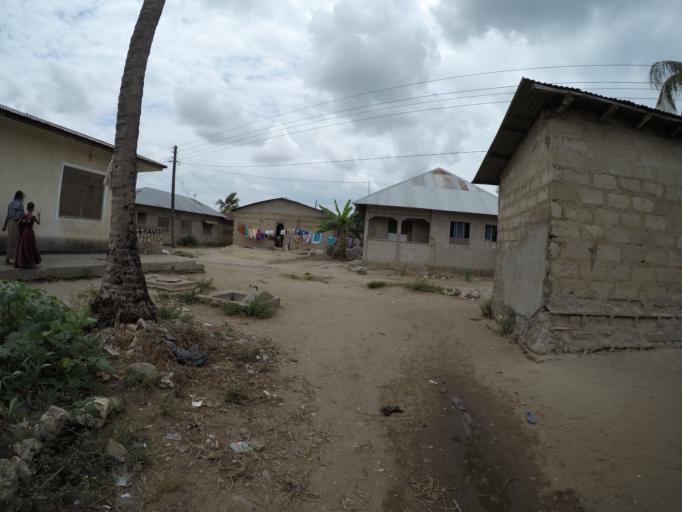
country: TZ
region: Zanzibar Urban/West
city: Zanzibar
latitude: -6.1787
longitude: 39.2084
